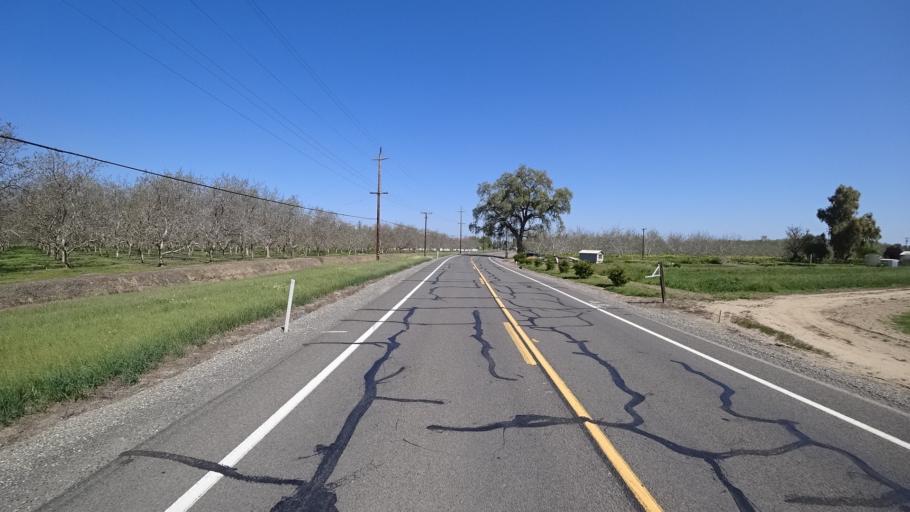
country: US
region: California
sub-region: Glenn County
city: Willows
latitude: 39.5175
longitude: -122.0157
